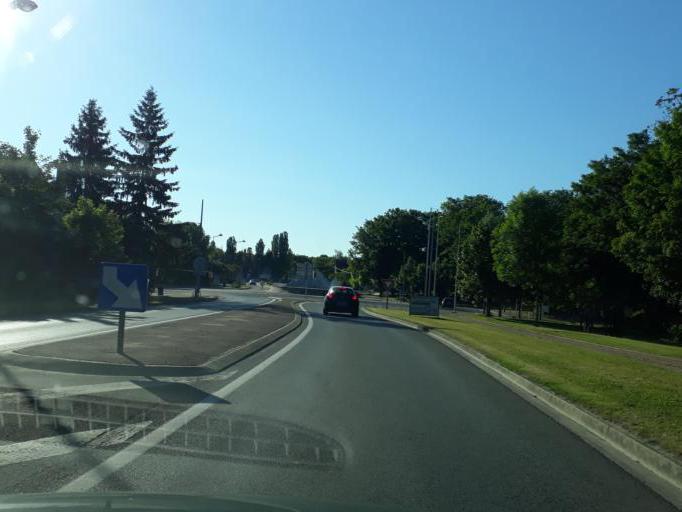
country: FR
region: Bourgogne
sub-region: Departement de la Nievre
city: Neuvy-sur-Loire
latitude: 47.5235
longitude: 2.8759
